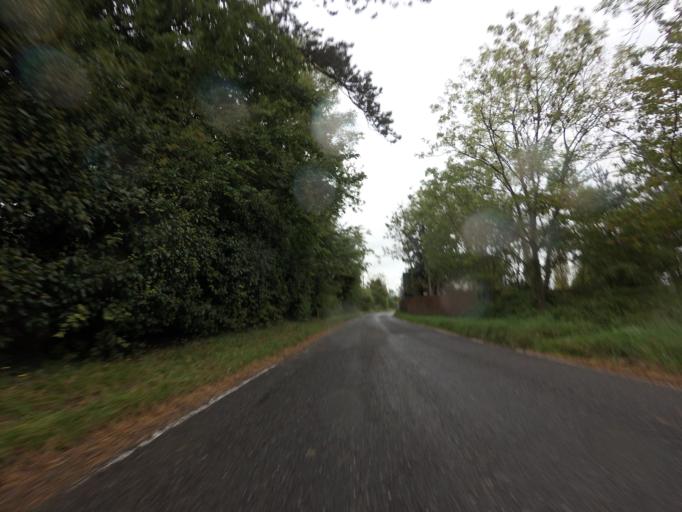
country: GB
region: England
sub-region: Cambridgeshire
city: Comberton
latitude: 52.1652
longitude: -0.0117
